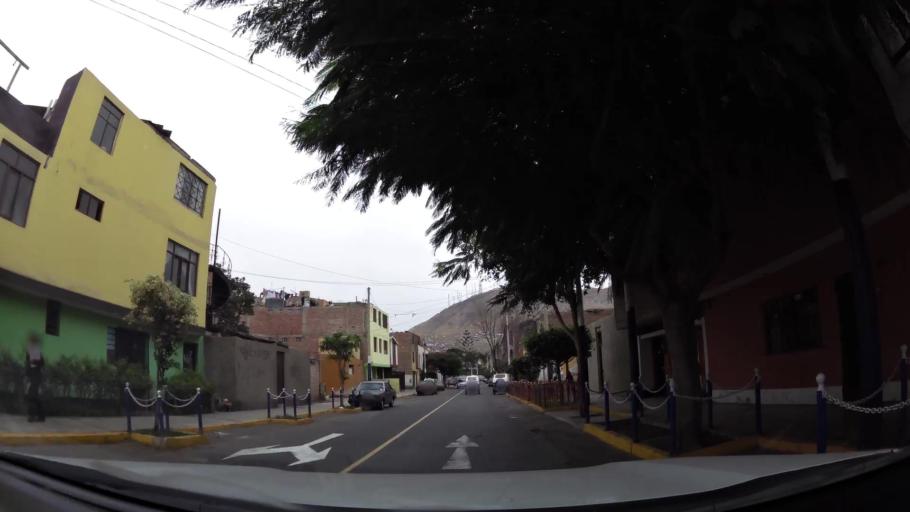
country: PE
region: Lima
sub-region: Lima
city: Surco
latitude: -12.1705
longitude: -77.0244
